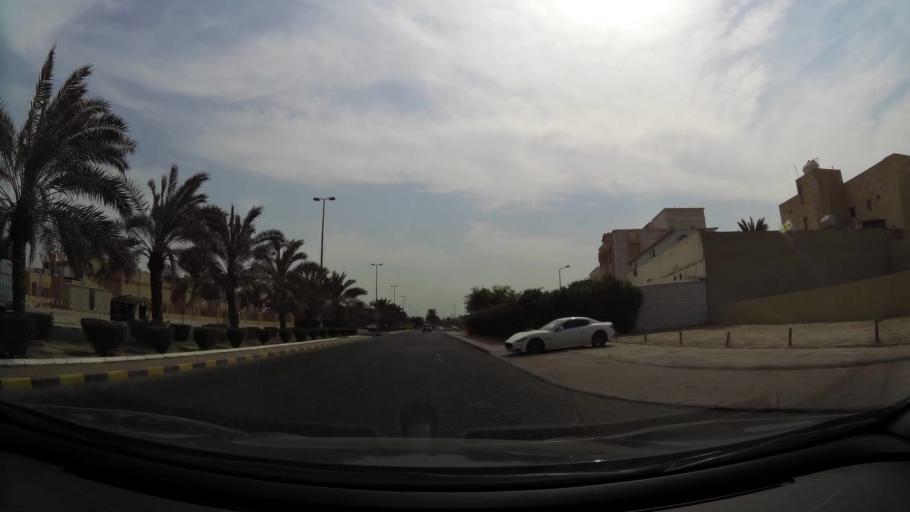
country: KW
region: Al Asimah
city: Ash Shamiyah
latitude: 29.3429
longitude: 47.9799
